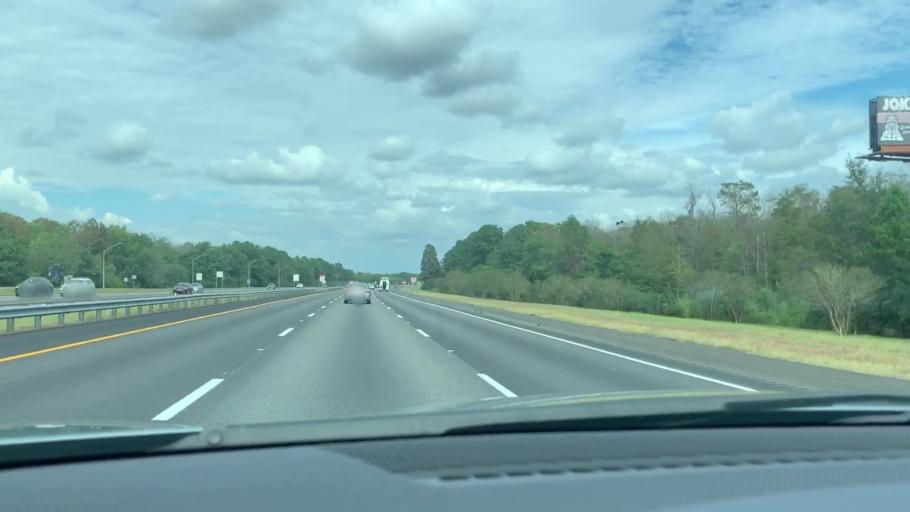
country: US
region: Georgia
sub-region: Chatham County
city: Port Wentworth
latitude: 32.2223
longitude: -81.1684
